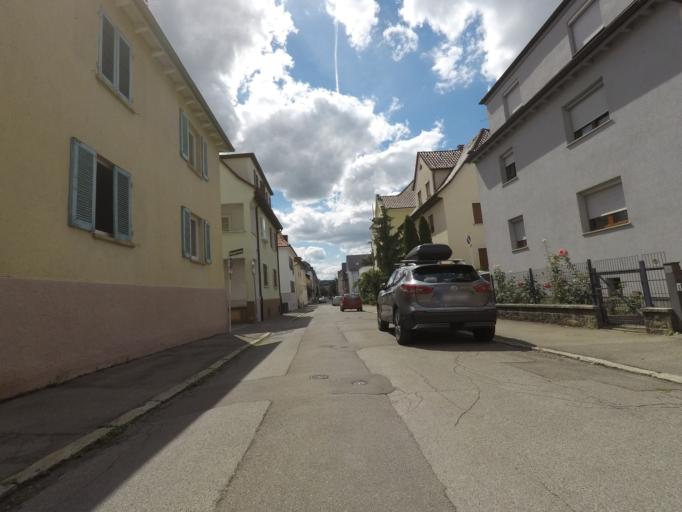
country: DE
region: Baden-Wuerttemberg
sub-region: Tuebingen Region
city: Reutlingen
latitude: 48.4901
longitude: 9.2262
